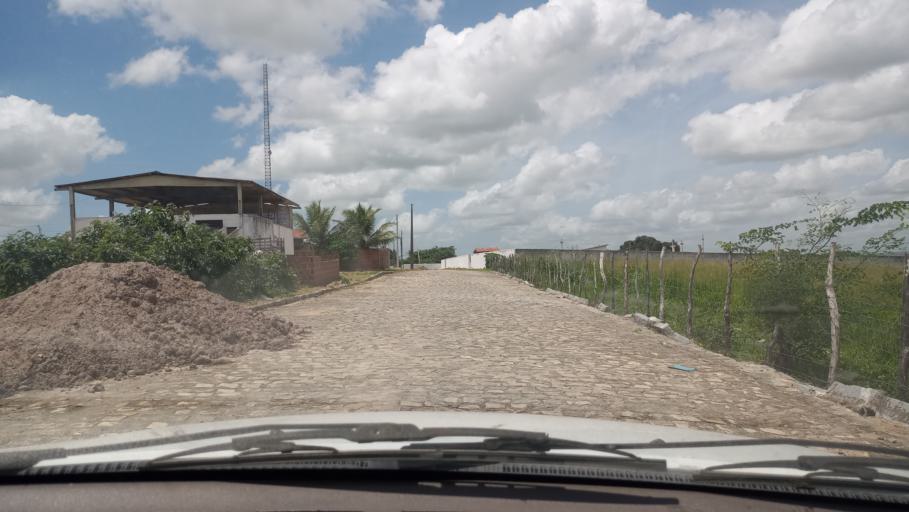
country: BR
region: Rio Grande do Norte
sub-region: Brejinho
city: Brejinho
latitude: -6.2692
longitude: -35.3745
